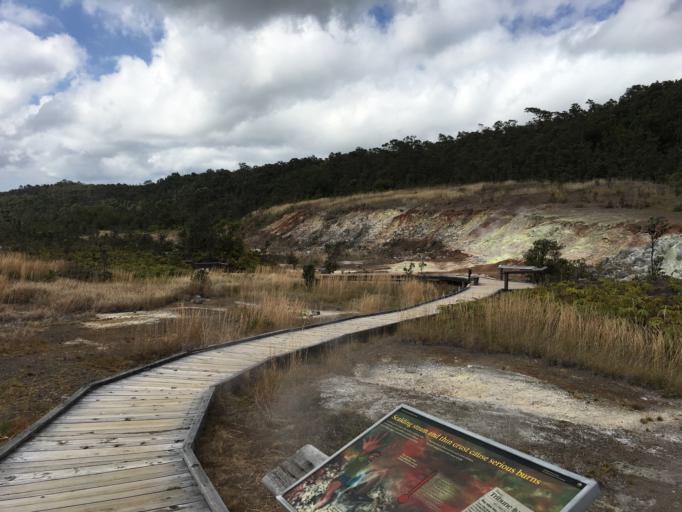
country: US
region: Hawaii
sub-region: Hawaii County
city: Volcano
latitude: 19.4316
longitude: -155.2609
